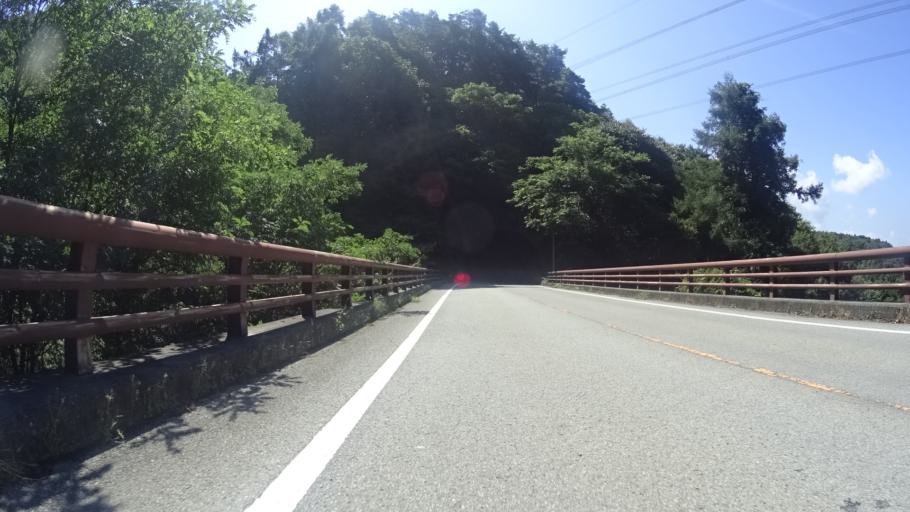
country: JP
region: Yamanashi
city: Enzan
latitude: 35.7447
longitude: 138.8090
